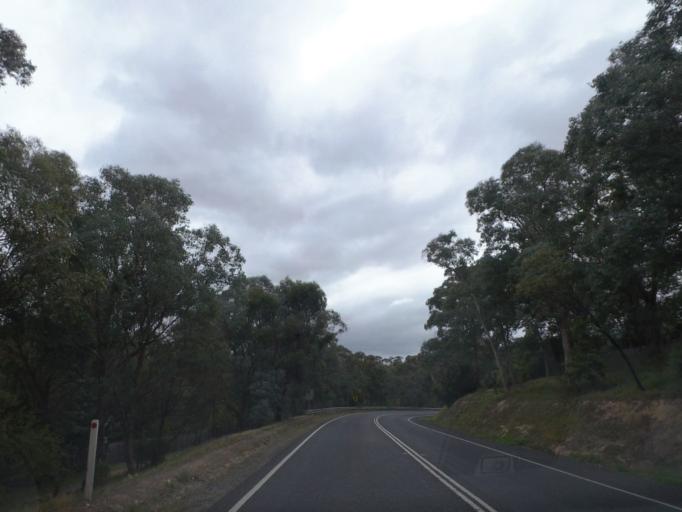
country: AU
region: Victoria
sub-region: Nillumbik
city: North Warrandyte
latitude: -37.7473
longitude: 145.2003
